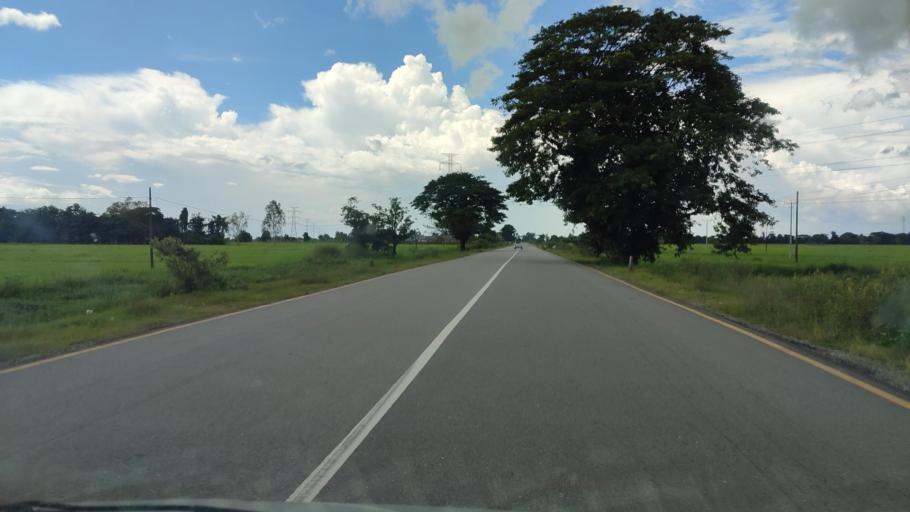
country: MM
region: Bago
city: Nyaunglebin
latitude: 18.0023
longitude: 96.7021
